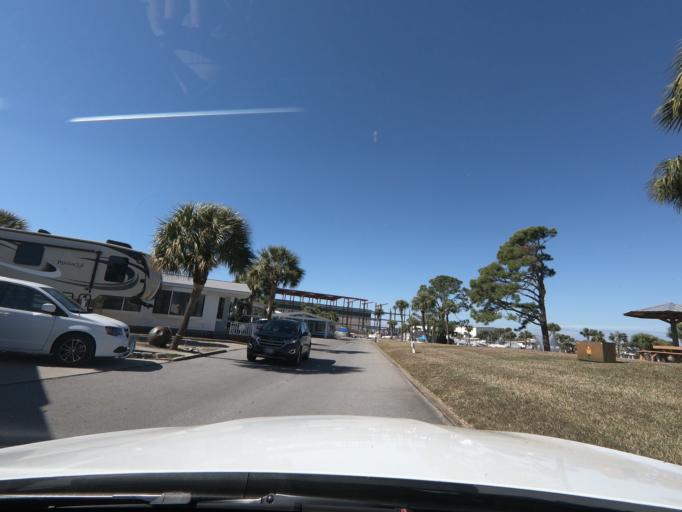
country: US
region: Florida
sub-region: Bay County
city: Lower Grand Lagoon
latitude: 30.1418
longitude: -85.7458
